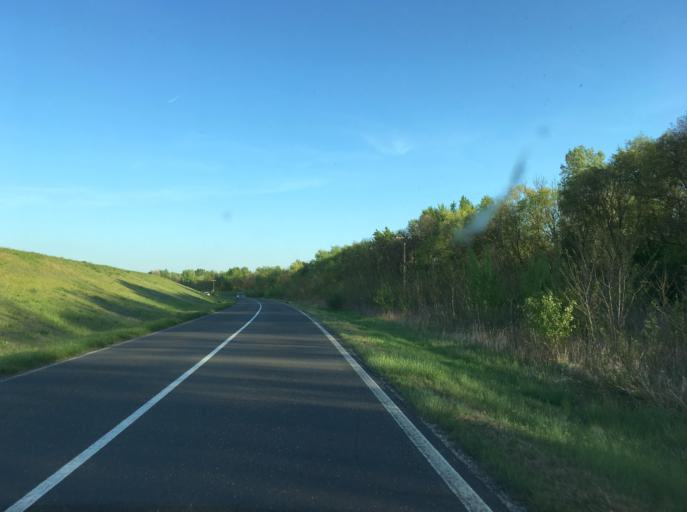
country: HU
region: Gyor-Moson-Sopron
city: Rajka
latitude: 48.0051
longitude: 17.2537
